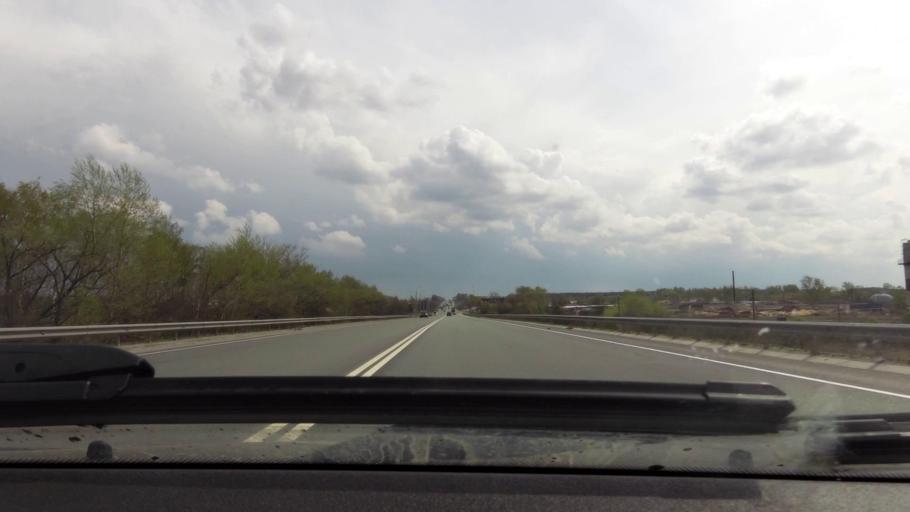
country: RU
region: Rjazan
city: Bagramovo
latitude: 54.7349
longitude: 39.4550
